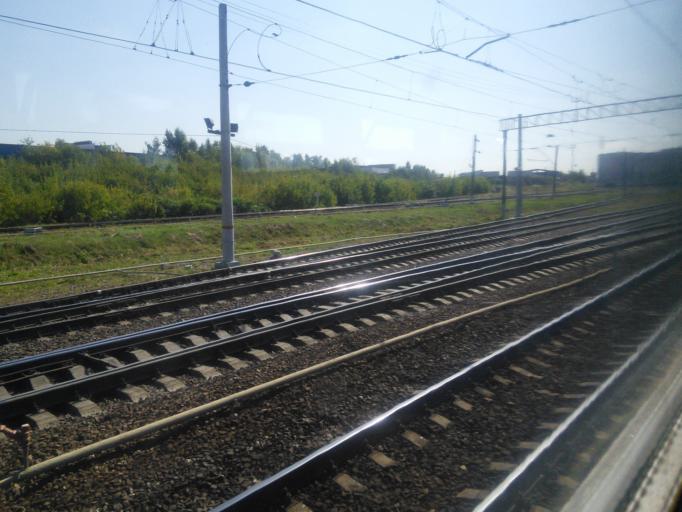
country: RU
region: Moskovskaya
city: Biryulevo Zapadnoye
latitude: 55.5974
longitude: 37.6243
